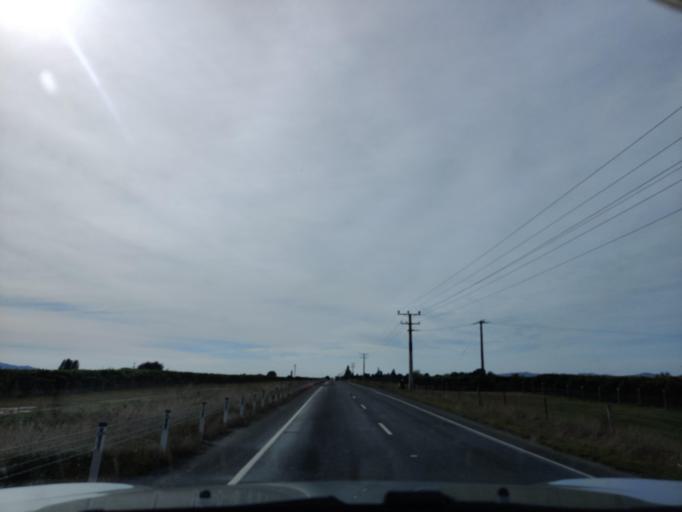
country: NZ
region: Marlborough
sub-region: Marlborough District
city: Blenheim
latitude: -41.5160
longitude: 173.7820
